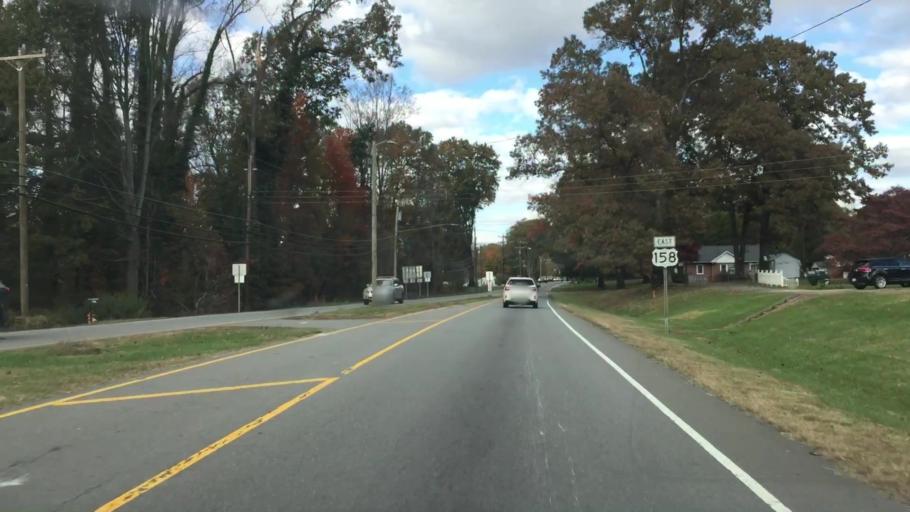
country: US
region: North Carolina
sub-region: Forsyth County
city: Winston-Salem
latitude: 36.1162
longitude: -80.1862
